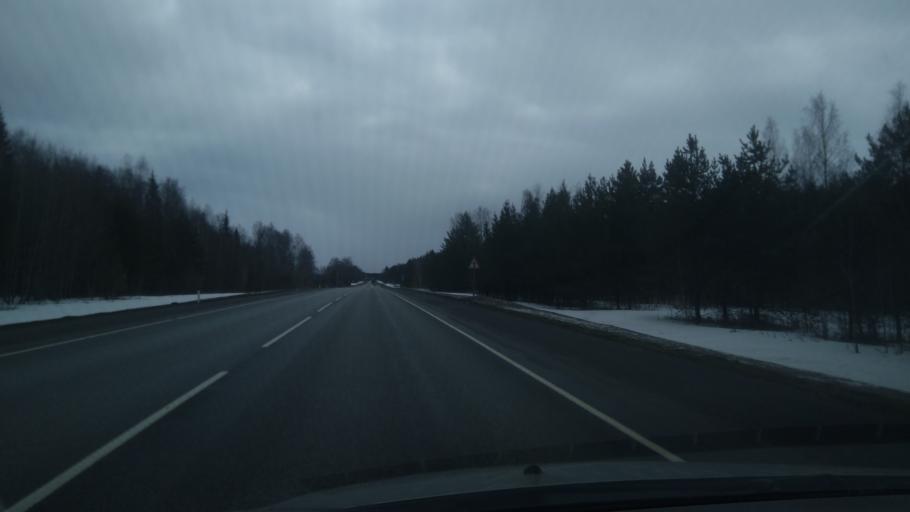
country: RU
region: Perm
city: Suksun
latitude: 56.9205
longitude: 57.5699
